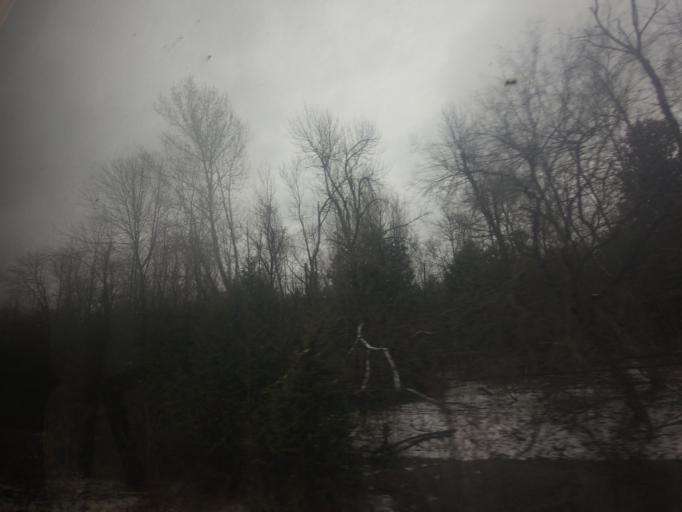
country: CA
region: Ontario
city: Cobourg
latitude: 43.9581
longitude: -78.1927
